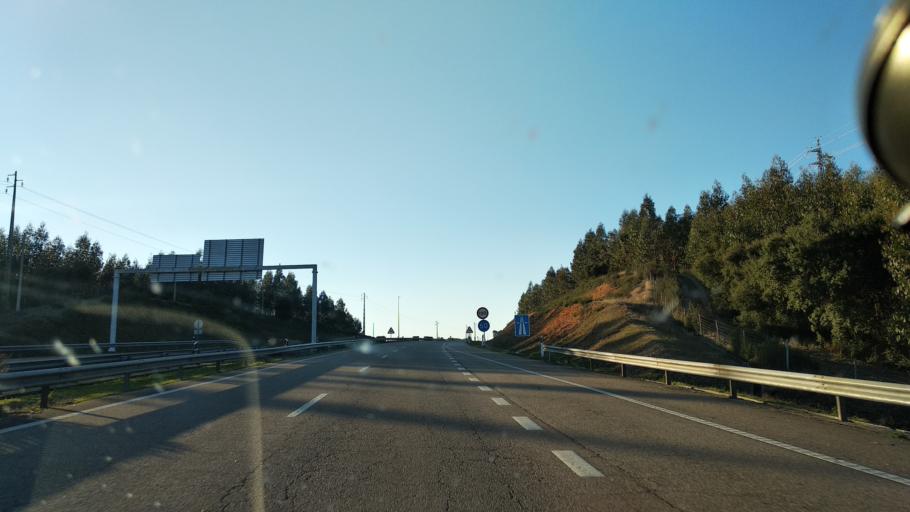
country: PT
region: Santarem
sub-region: Abrantes
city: Tramagal
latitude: 39.4863
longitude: -8.2785
